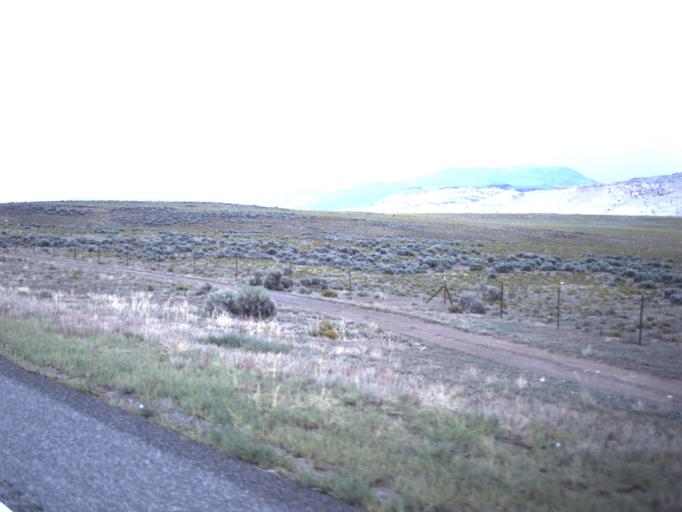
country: US
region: Utah
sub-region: Piute County
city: Junction
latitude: 38.2717
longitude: -112.2228
